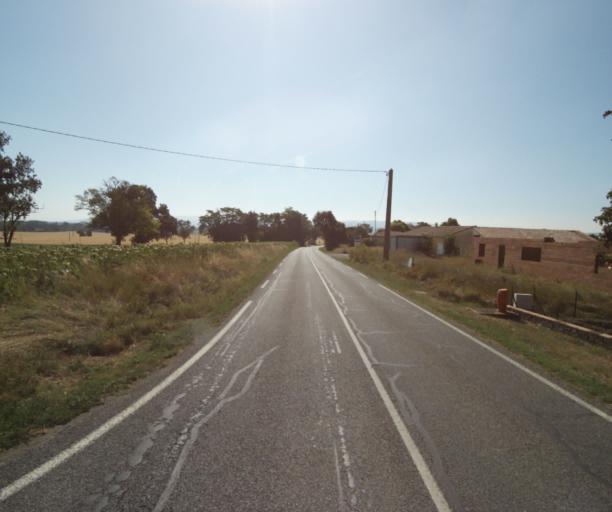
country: FR
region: Midi-Pyrenees
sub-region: Departement de la Haute-Garonne
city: Saint-Felix-Lauragais
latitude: 43.4776
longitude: 1.9259
